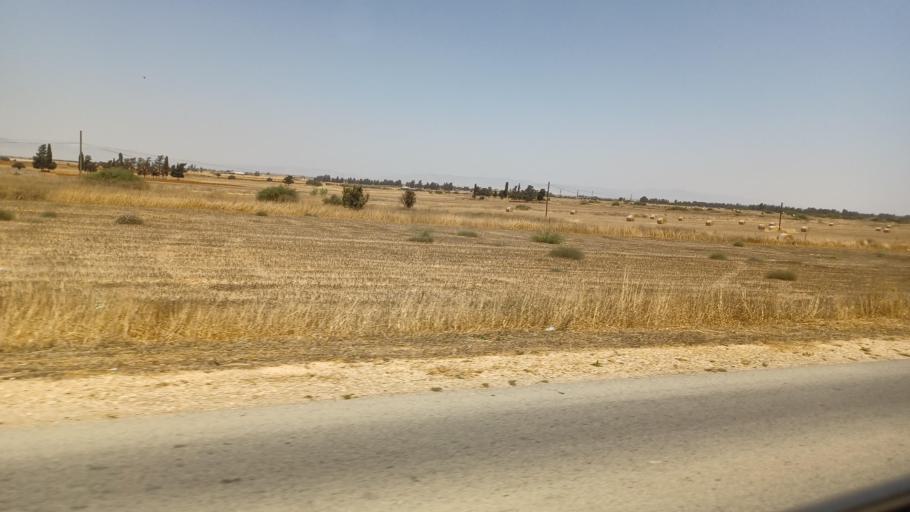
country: CY
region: Ammochostos
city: Achna
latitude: 35.0616
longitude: 33.8003
